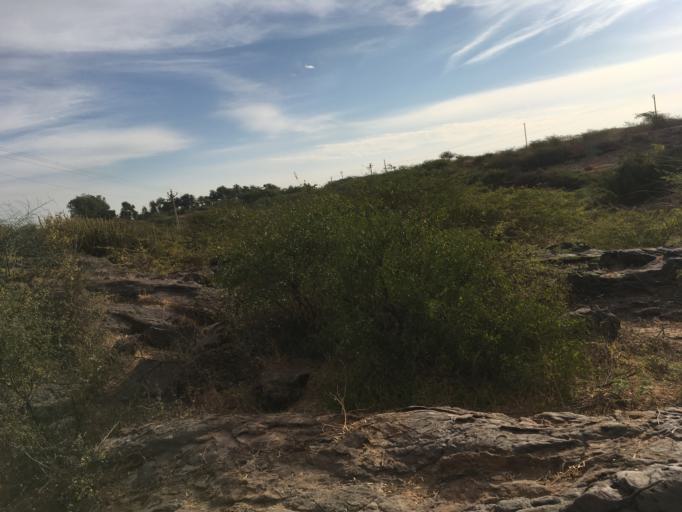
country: IN
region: Gujarat
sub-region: Kachchh
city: Bhuj
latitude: 23.2504
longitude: 69.6282
